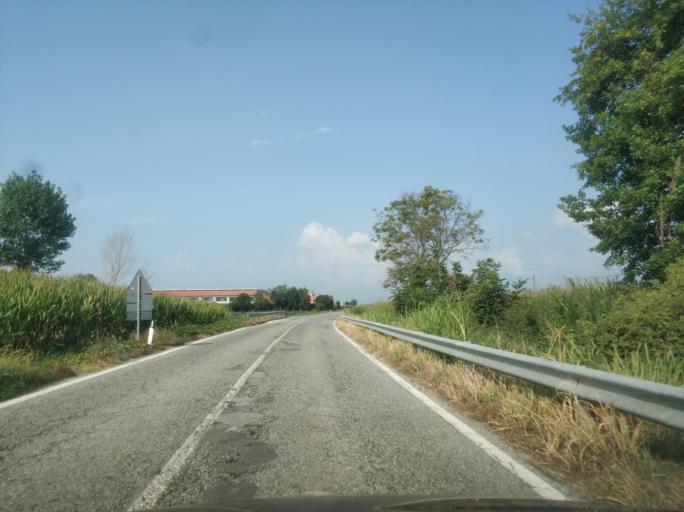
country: IT
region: Piedmont
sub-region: Provincia di Cuneo
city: Centallo
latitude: 44.5117
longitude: 7.6387
